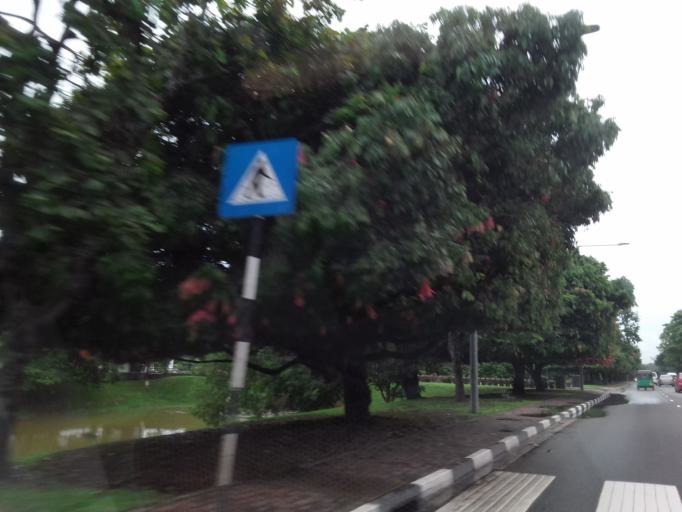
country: LK
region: Western
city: Battaramulla South
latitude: 6.9010
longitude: 79.9120
